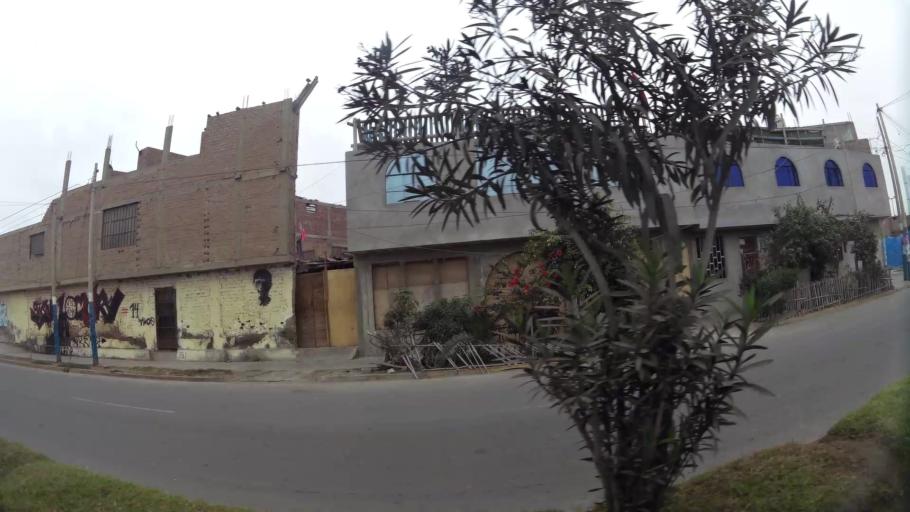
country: PE
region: Ica
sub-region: Provincia de Pisco
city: Pisco
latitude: -13.7138
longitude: -76.2096
